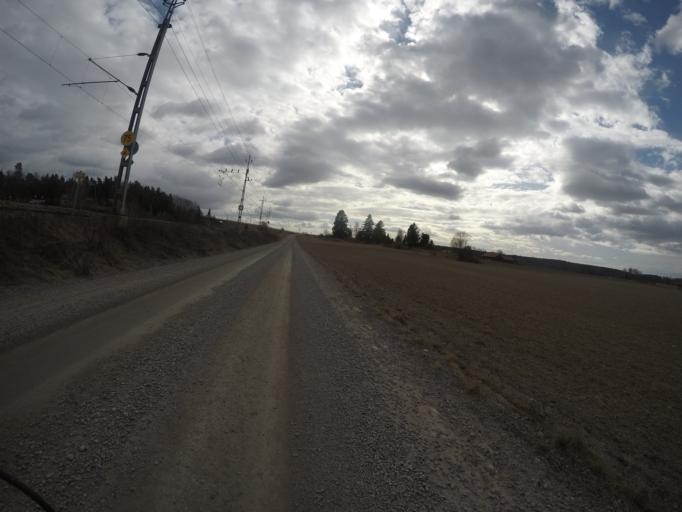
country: SE
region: Soedermanland
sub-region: Eskilstuna Kommun
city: Kvicksund
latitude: 59.4313
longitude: 16.3354
